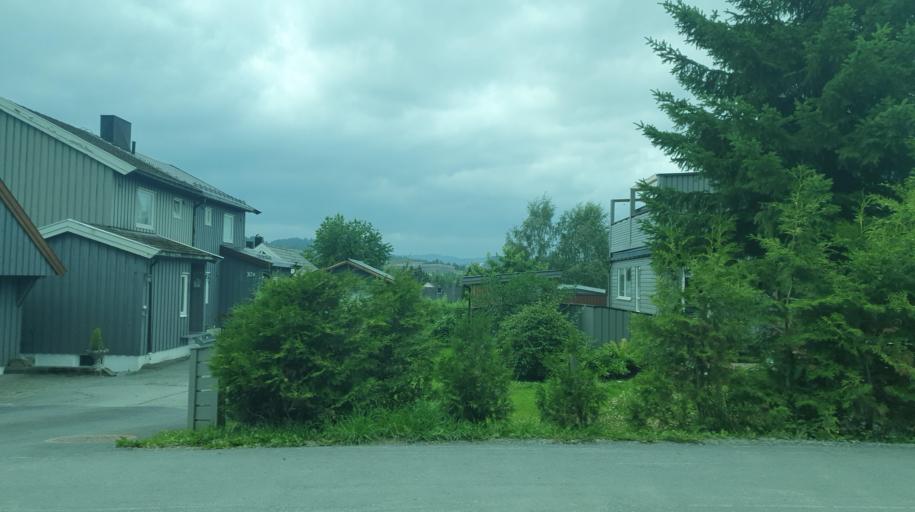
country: NO
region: Sor-Trondelag
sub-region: Trondheim
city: Trondheim
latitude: 63.3590
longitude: 10.3671
